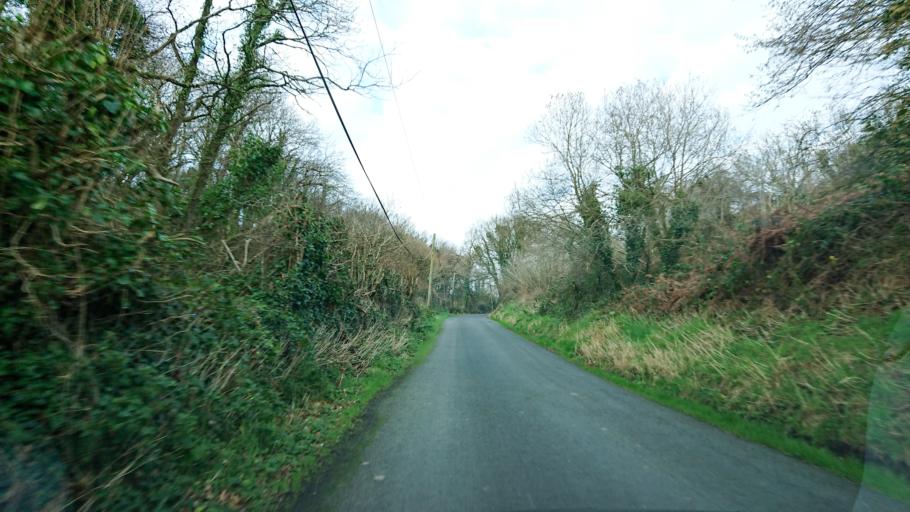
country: IE
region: Munster
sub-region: Waterford
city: Tra Mhor
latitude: 52.1575
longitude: -7.2676
